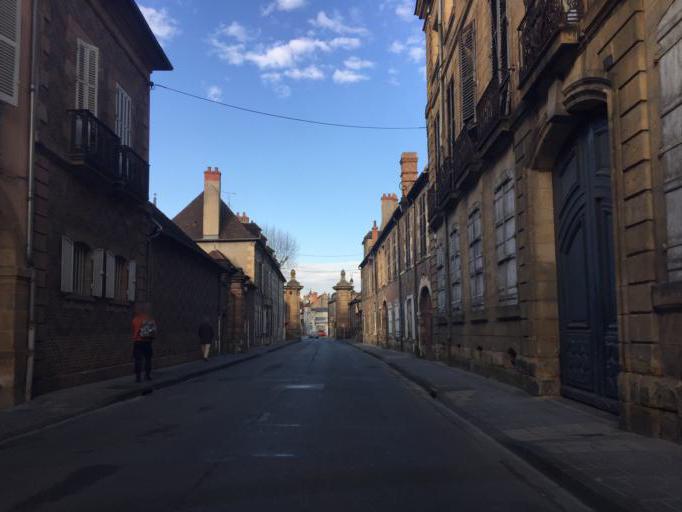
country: FR
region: Auvergne
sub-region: Departement de l'Allier
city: Moulins
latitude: 46.5697
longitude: 3.3295
